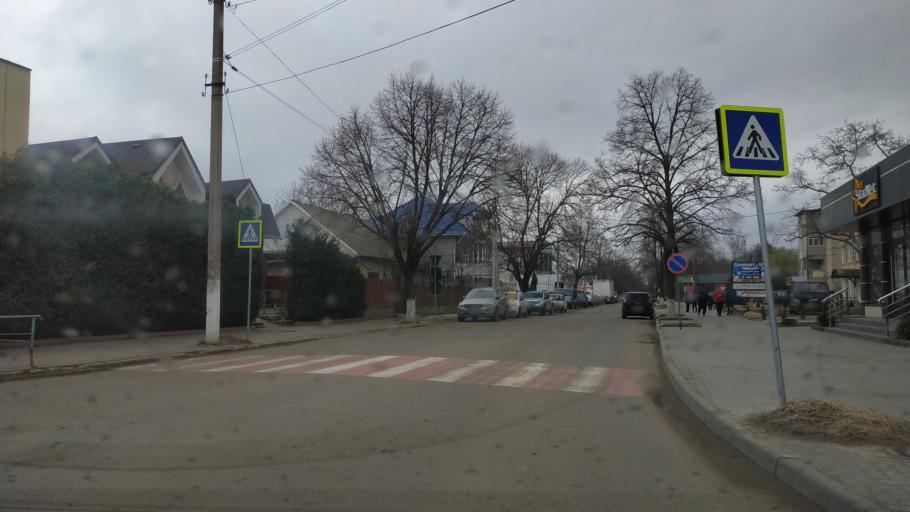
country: MD
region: Leova
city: Leova
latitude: 46.4839
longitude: 28.2507
